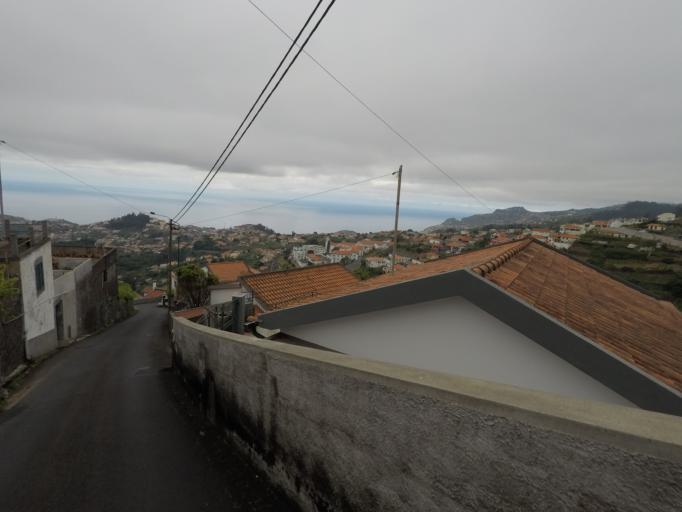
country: PT
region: Madeira
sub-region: Funchal
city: Nossa Senhora do Monte
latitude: 32.6805
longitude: -16.9431
